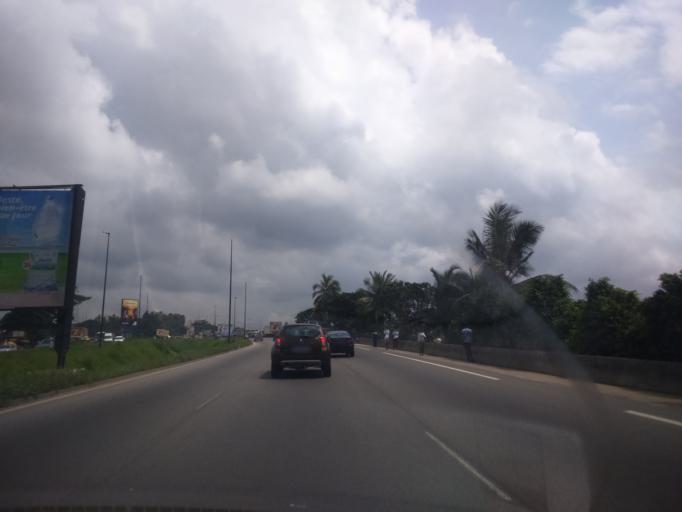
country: CI
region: Lagunes
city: Abobo
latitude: 5.3640
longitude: -4.0258
